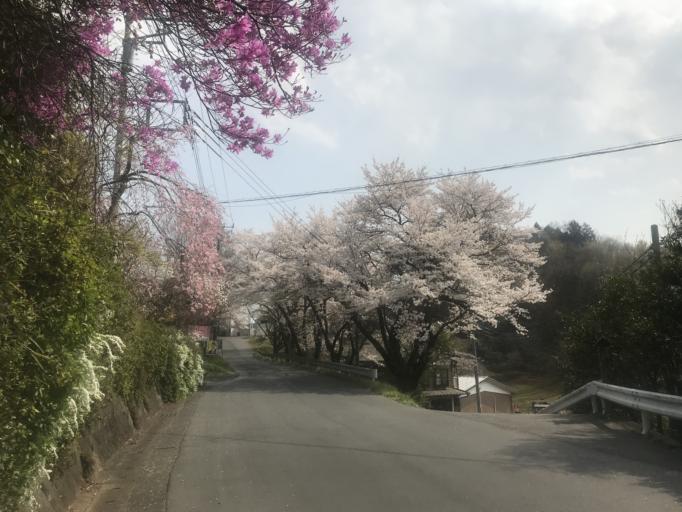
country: JP
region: Yamanashi
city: Uenohara
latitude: 35.5957
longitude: 139.1639
